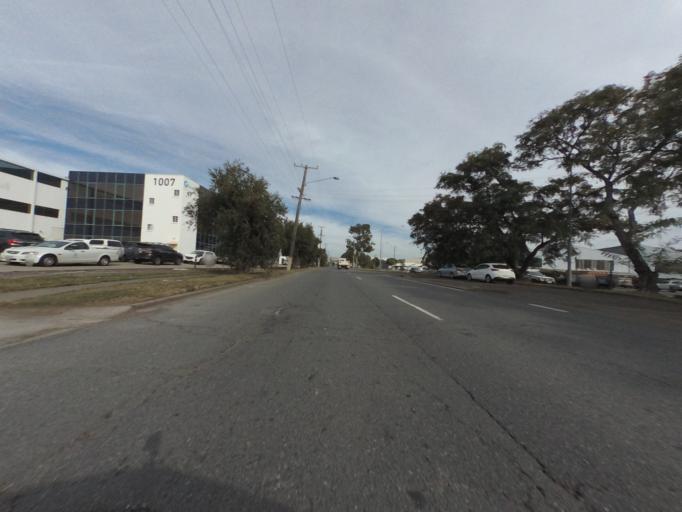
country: AU
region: Queensland
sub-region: Brisbane
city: Ascot
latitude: -27.4292
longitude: 153.0967
